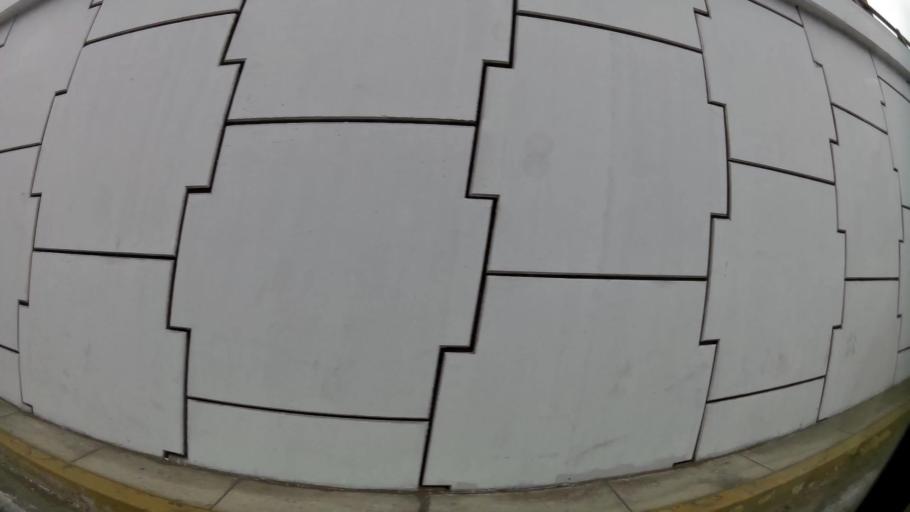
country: PE
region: Callao
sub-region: Callao
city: Callao
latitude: -12.0583
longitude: -77.1293
